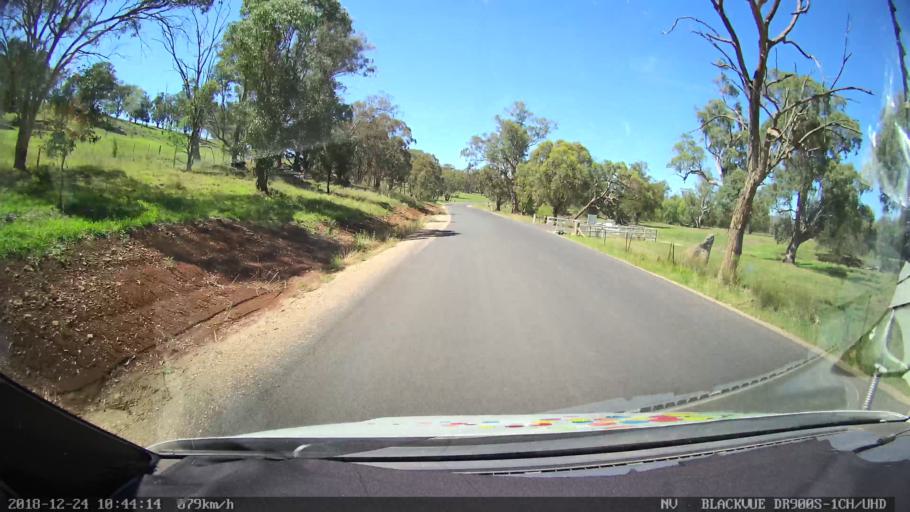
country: AU
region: New South Wales
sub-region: Upper Hunter Shire
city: Merriwa
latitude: -31.8907
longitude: 150.4439
